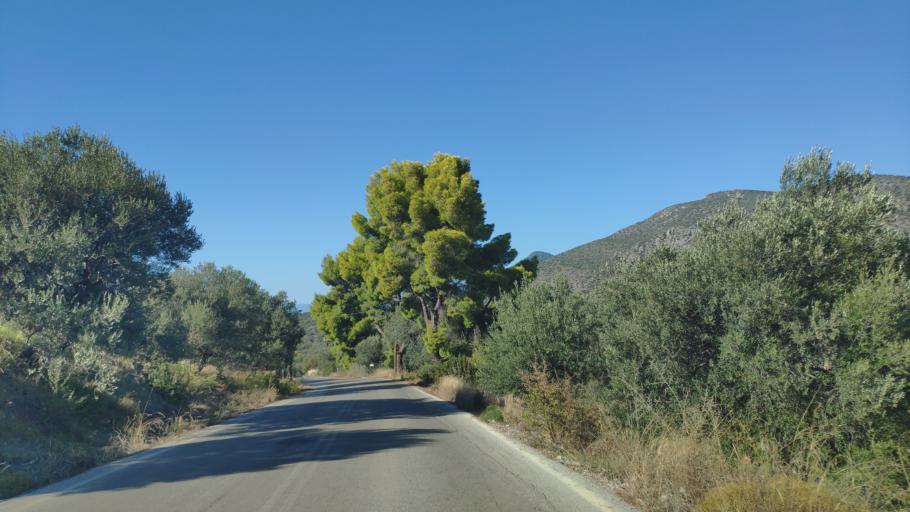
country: GR
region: Attica
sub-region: Nomos Piraios
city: Galatas
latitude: 37.5475
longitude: 23.3757
